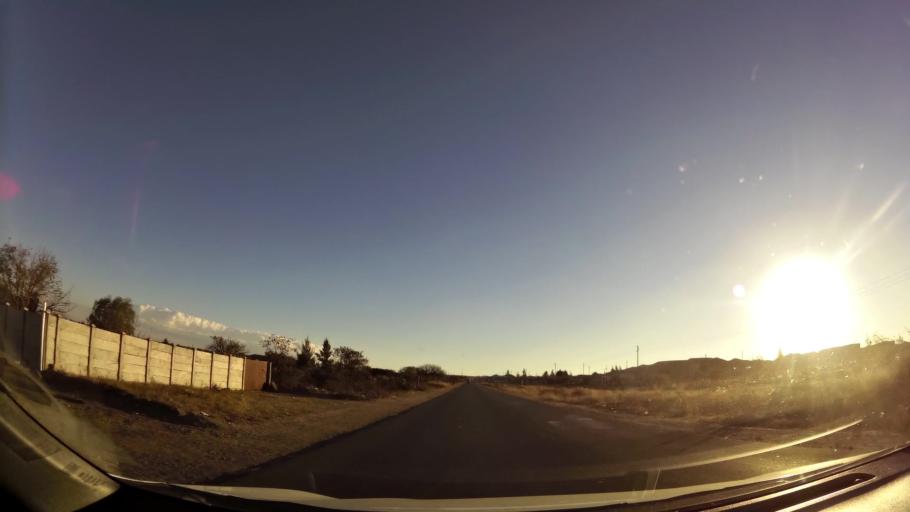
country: ZA
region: Limpopo
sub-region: Capricorn District Municipality
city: Polokwane
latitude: -23.8377
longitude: 29.3546
